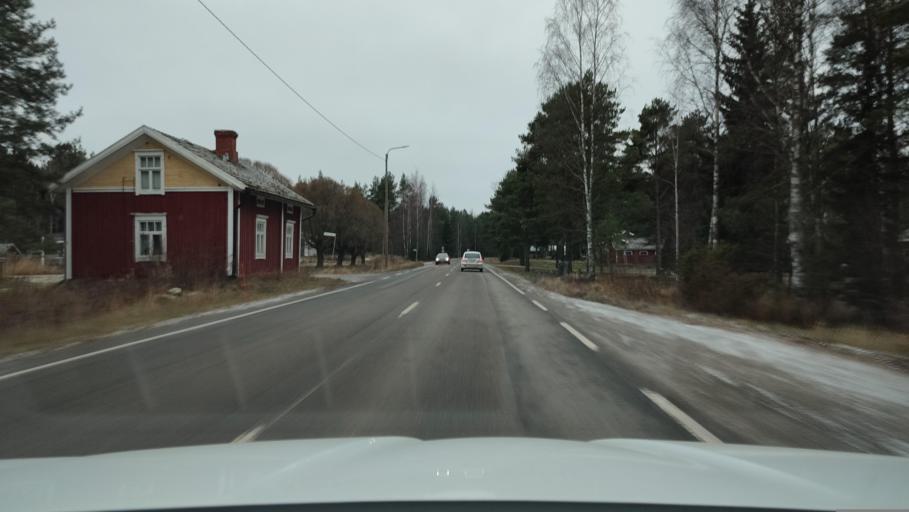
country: FI
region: Ostrobothnia
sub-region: Sydosterbotten
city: Naerpes
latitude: 62.3948
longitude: 21.3710
